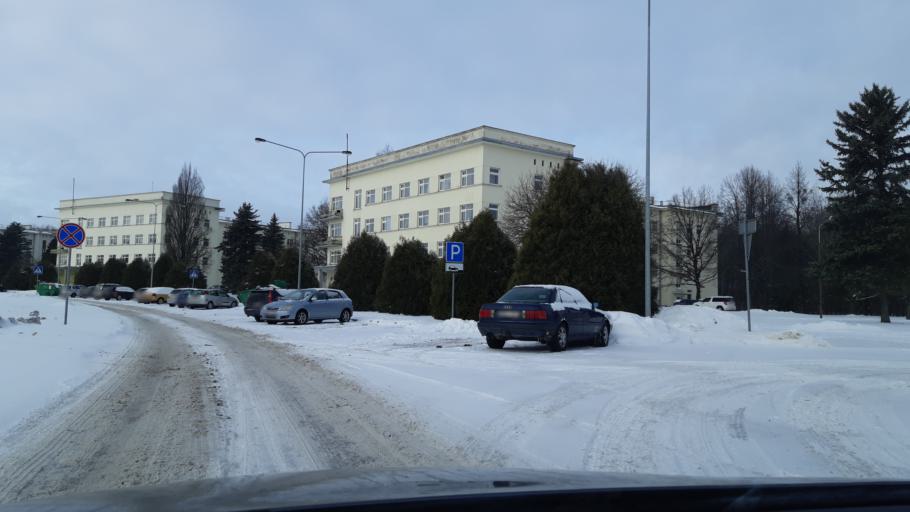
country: LT
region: Kauno apskritis
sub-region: Kauno rajonas
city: Akademija (Kaunas)
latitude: 54.8939
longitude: 23.8340
